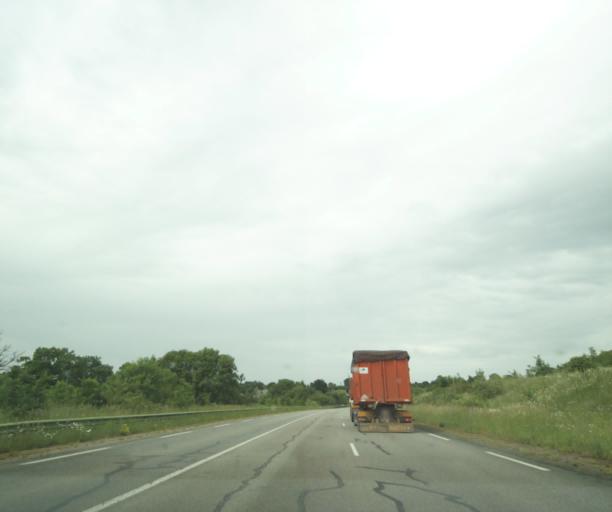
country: FR
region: Poitou-Charentes
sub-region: Departement des Deux-Sevres
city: Le Tallud
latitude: 46.6353
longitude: -0.2765
